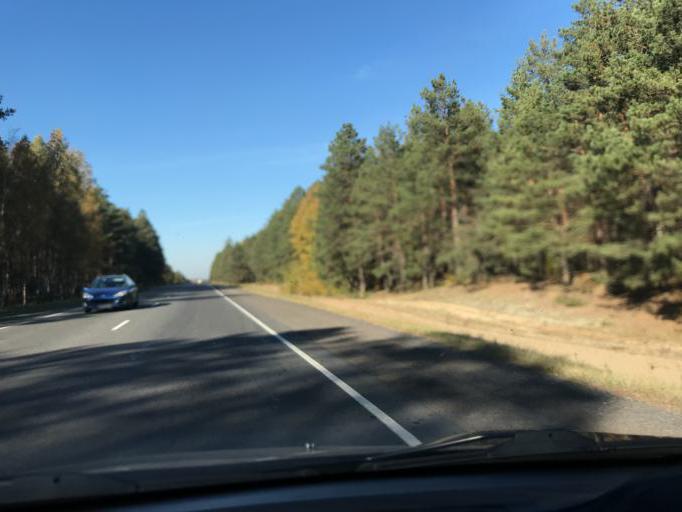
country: BY
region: Gomel
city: Kalinkavichy
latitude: 52.3608
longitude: 29.3707
